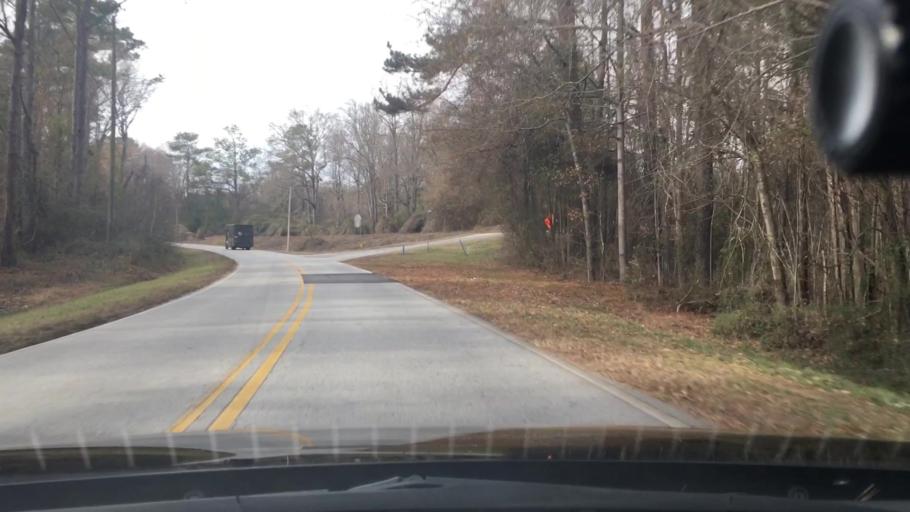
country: US
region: Georgia
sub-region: Spalding County
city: Experiment
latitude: 33.2794
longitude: -84.3765
